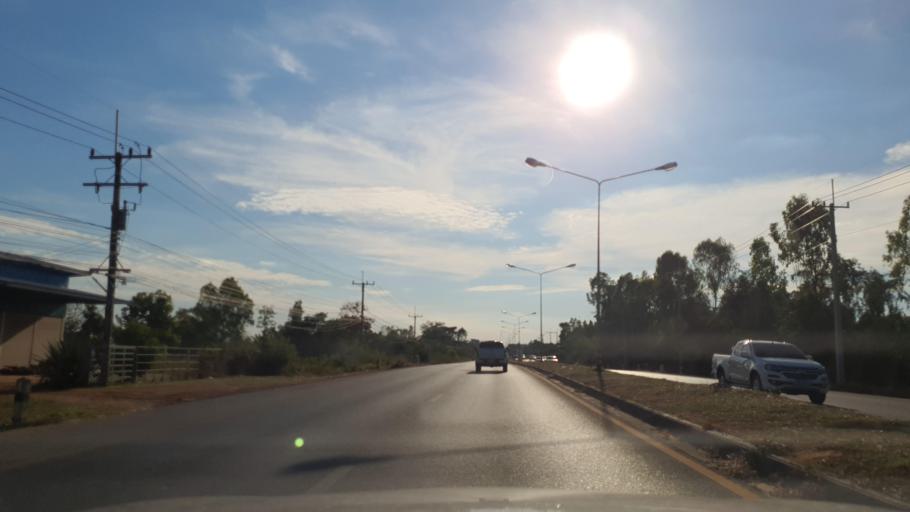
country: TH
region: Maha Sarakham
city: Kantharawichai
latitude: 16.3421
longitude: 103.3161
